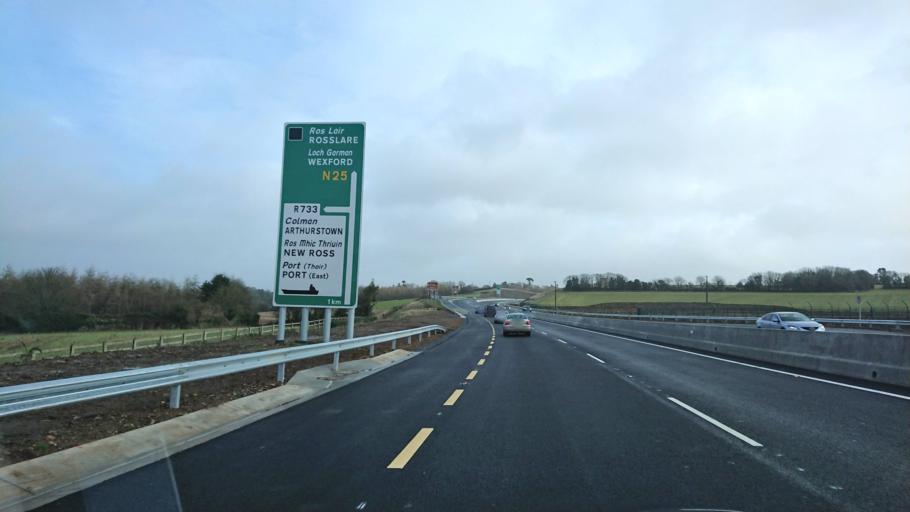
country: IE
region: Leinster
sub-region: Loch Garman
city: New Ross
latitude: 52.3572
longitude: -6.9847
